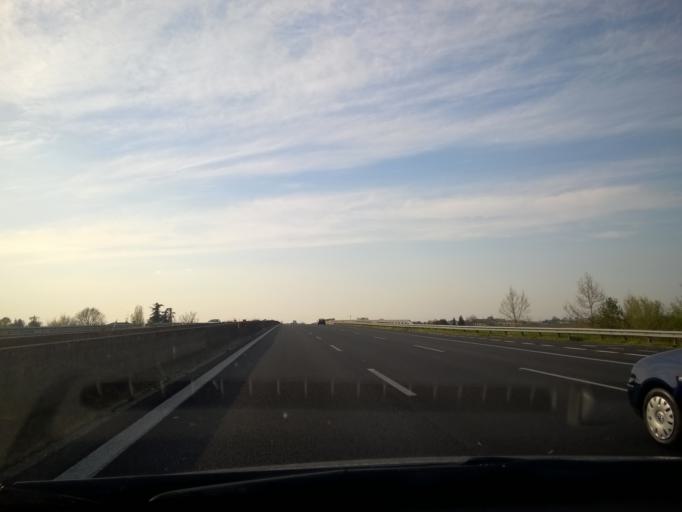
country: IT
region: Emilia-Romagna
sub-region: Forli-Cesena
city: Forlimpopoli
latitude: 44.2369
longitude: 12.1342
